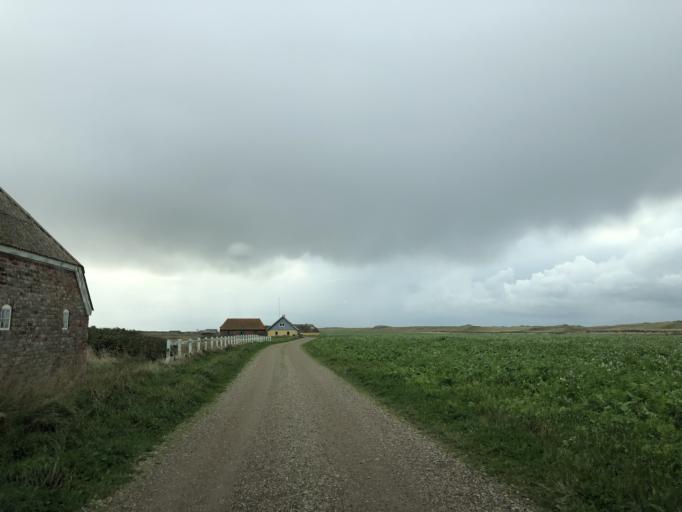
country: DK
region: Central Jutland
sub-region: Lemvig Kommune
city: Harboore
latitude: 56.4716
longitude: 8.1311
